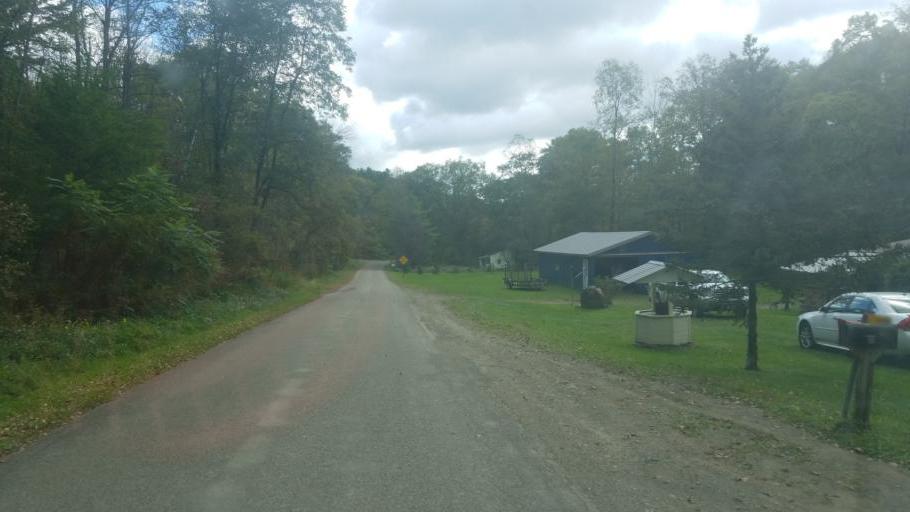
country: US
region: New York
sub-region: Allegany County
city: Cuba
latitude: 42.2190
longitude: -78.3336
